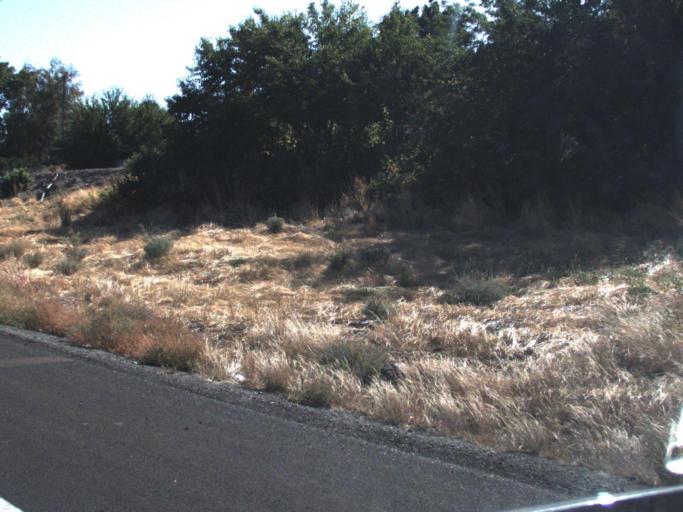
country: US
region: Washington
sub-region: Franklin County
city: West Pasco
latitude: 46.2321
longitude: -119.2142
